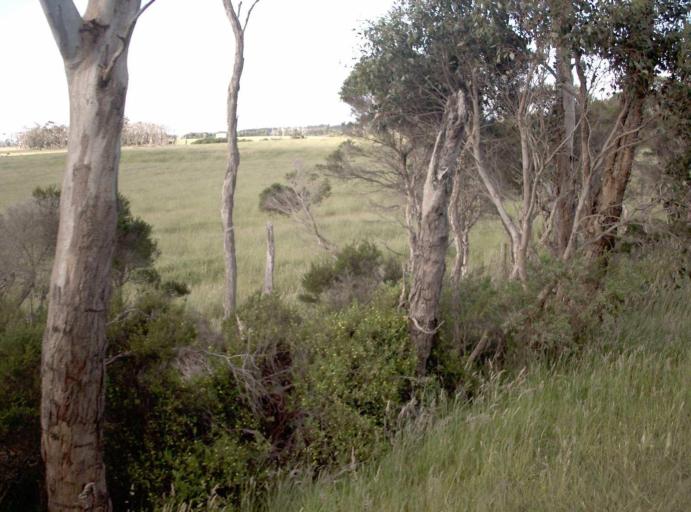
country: AU
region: Victoria
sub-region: Bass Coast
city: North Wonthaggi
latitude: -38.5955
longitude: 145.7882
